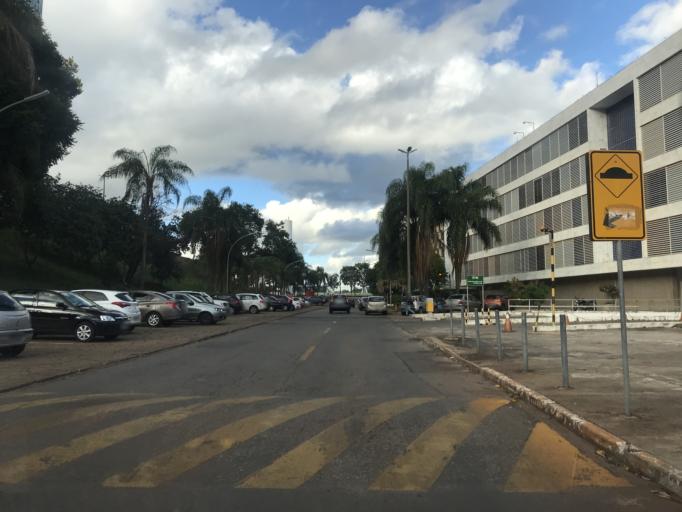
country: BR
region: Federal District
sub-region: Brasilia
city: Brasilia
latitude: -15.7994
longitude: -47.8805
